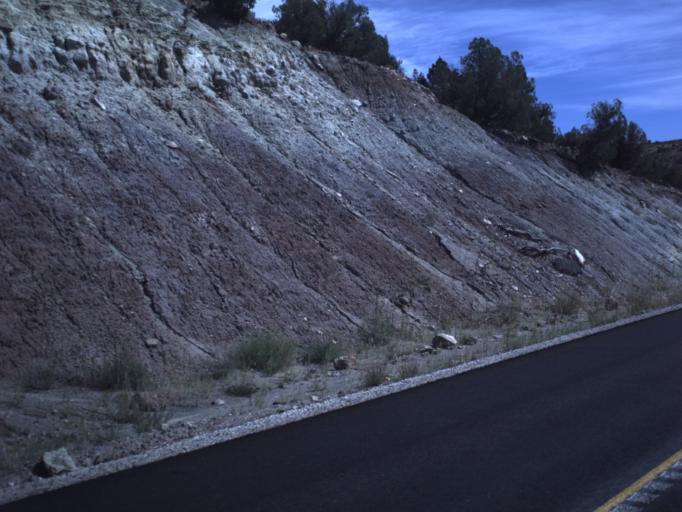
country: US
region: Utah
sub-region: San Juan County
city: Blanding
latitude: 37.5779
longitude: -109.5117
